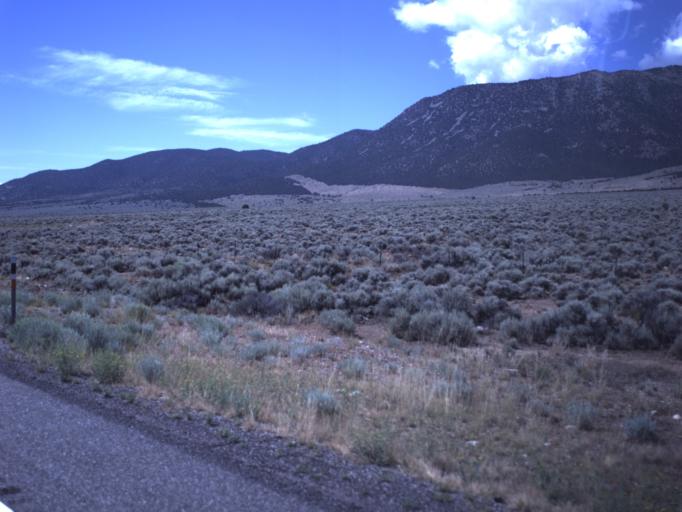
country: US
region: Utah
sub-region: Piute County
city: Junction
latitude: 38.3833
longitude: -112.2288
